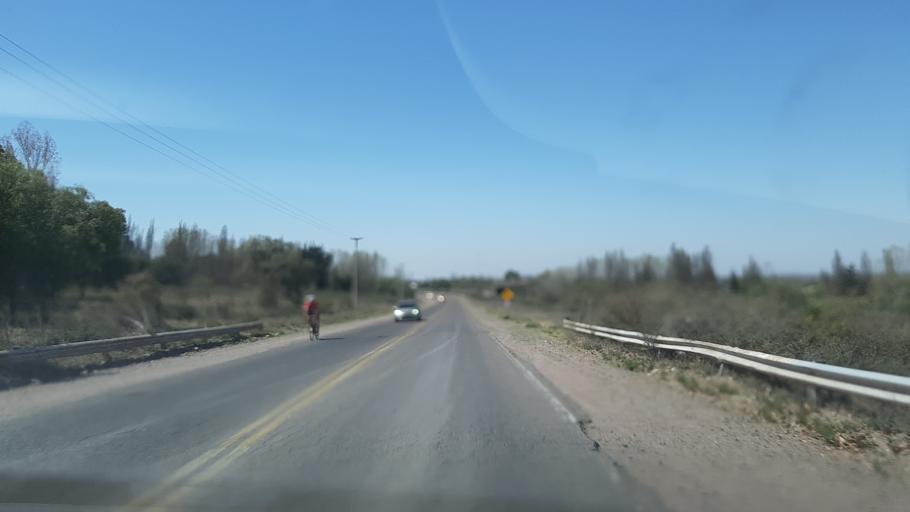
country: AR
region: Mendoza
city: Lujan de Cuyo
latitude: -33.0175
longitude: -68.9382
